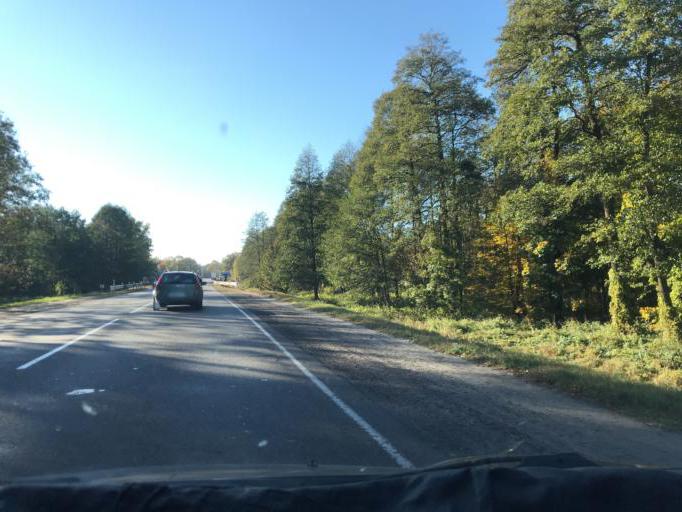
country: BY
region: Gomel
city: Kalinkavichy
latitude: 52.1236
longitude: 29.2867
